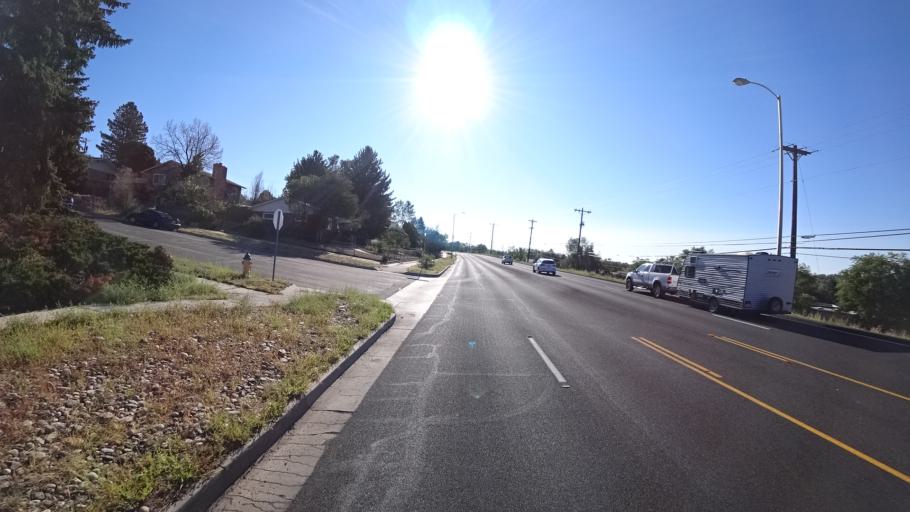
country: US
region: Colorado
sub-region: El Paso County
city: Colorado Springs
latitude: 38.8599
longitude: -104.7888
